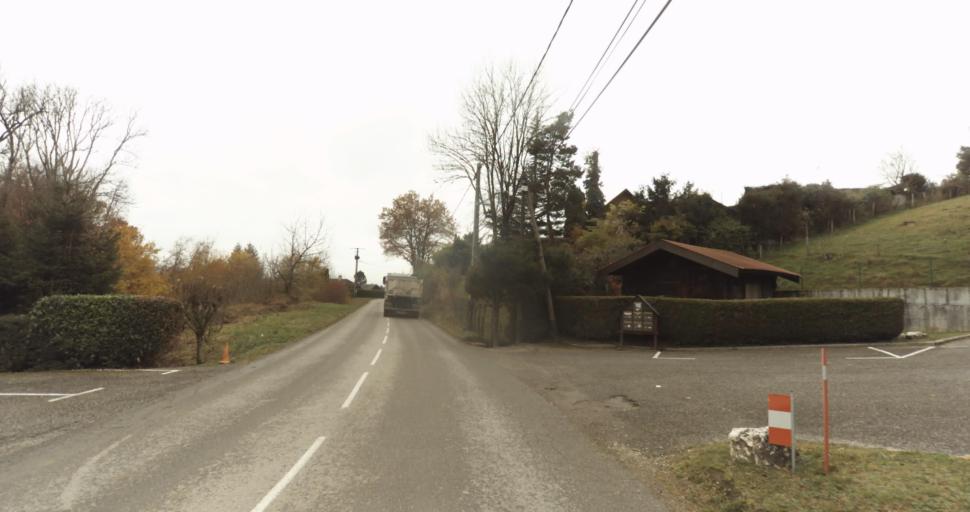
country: FR
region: Rhone-Alpes
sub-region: Departement de la Haute-Savoie
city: Groisy
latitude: 46.0150
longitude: 6.1828
